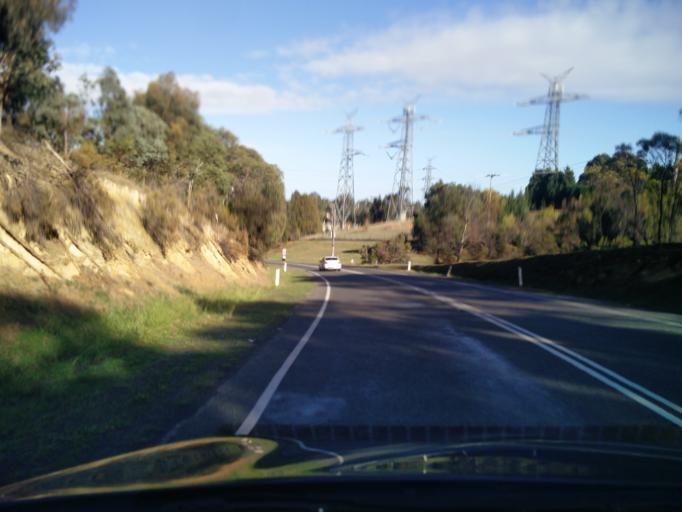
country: AU
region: Victoria
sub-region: Nillumbik
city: Eltham
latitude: -37.7478
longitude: 145.1798
